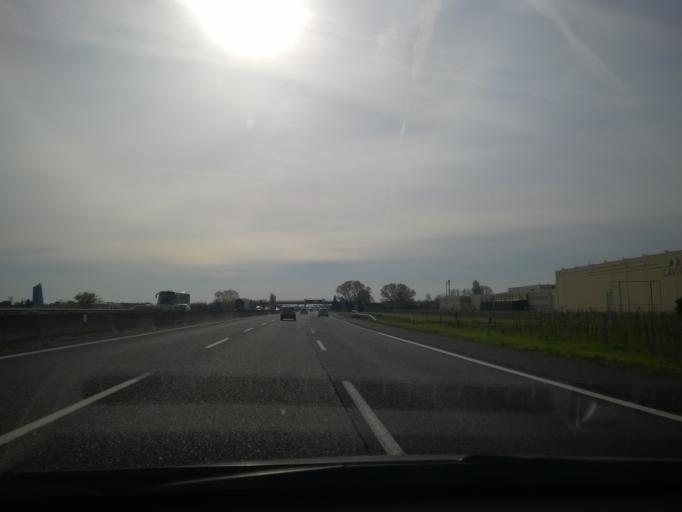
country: IT
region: Emilia-Romagna
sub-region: Forli-Cesena
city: Forli
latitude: 44.2586
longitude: 12.0740
